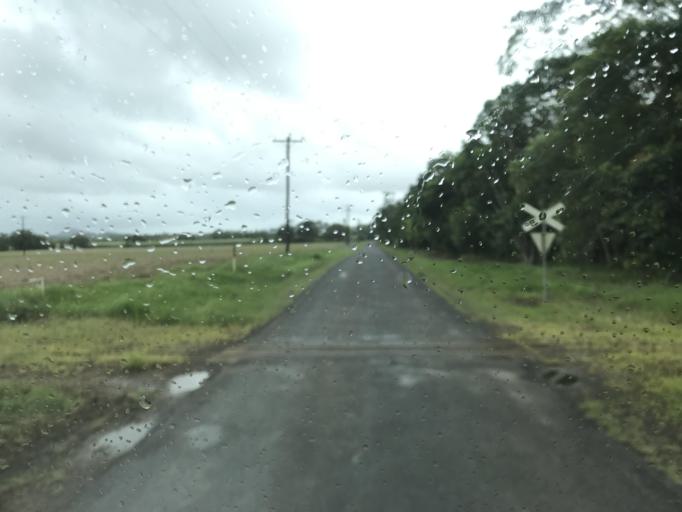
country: AU
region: Queensland
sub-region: Cassowary Coast
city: Innisfail
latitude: -17.4963
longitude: 145.9879
